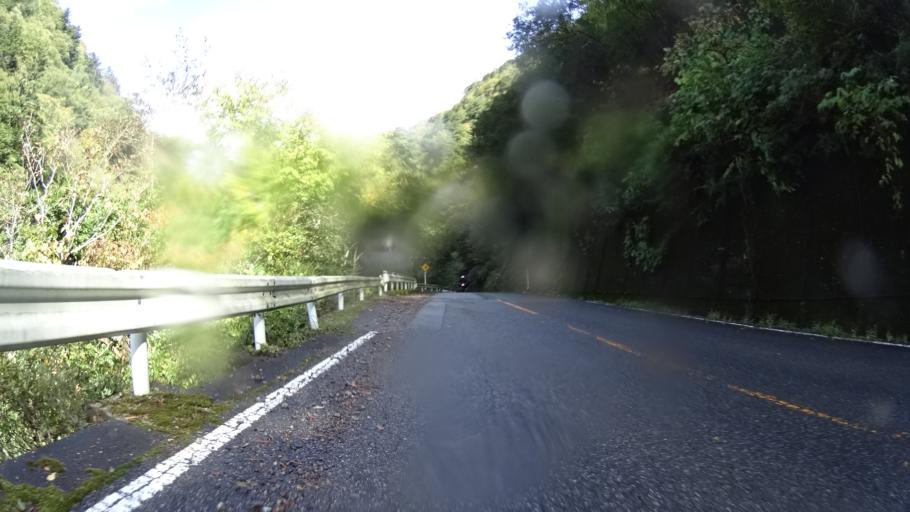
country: JP
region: Yamanashi
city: Enzan
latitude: 35.7975
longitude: 138.8655
